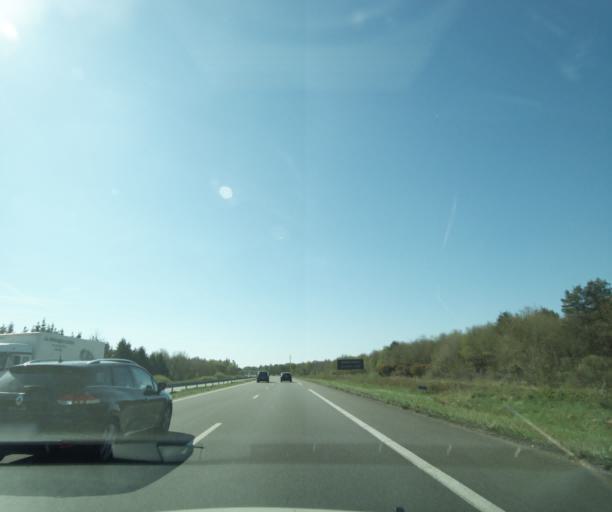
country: FR
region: Centre
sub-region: Departement du Loir-et-Cher
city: Salbris
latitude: 47.4569
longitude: 2.0043
